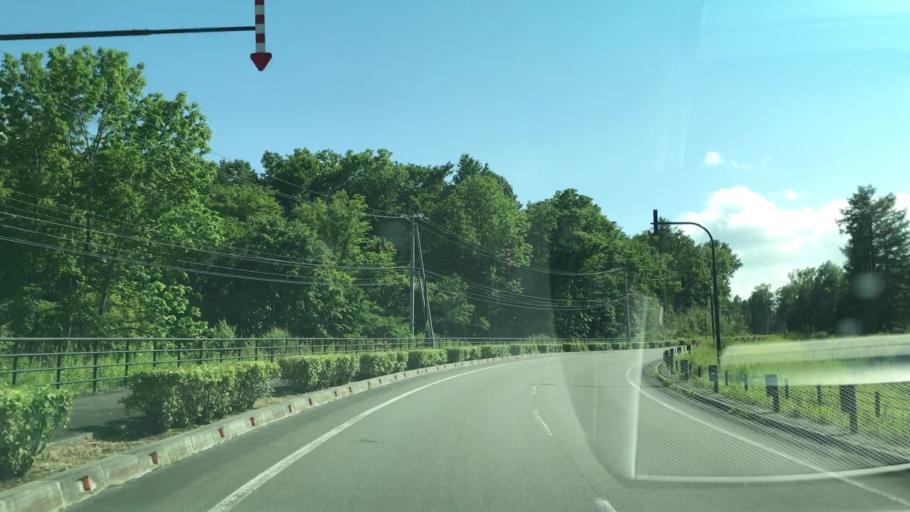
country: JP
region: Hokkaido
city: Shimo-furano
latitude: 42.8689
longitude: 142.4421
